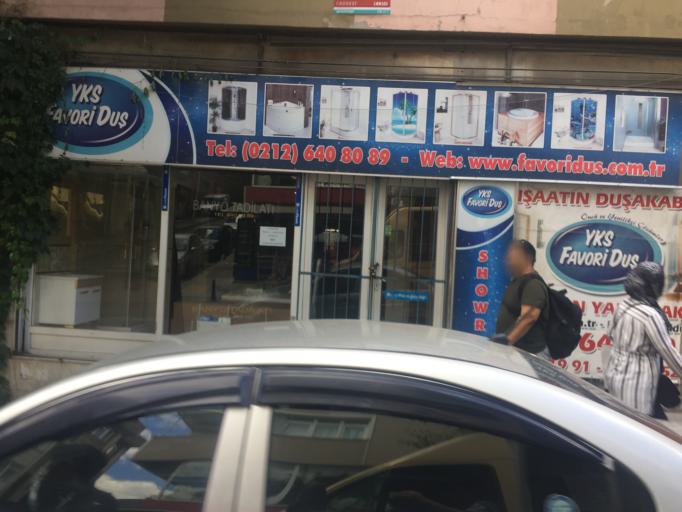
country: TR
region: Istanbul
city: Esenler
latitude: 41.0493
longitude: 28.9066
